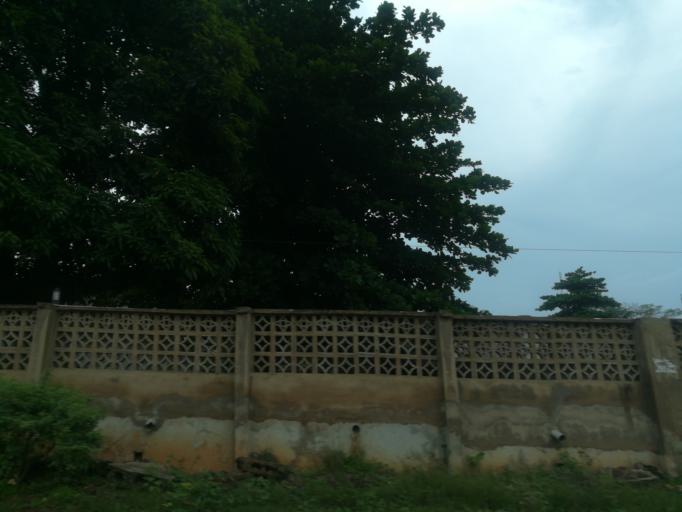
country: NG
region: Oyo
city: Ibadan
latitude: 7.4218
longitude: 3.9044
